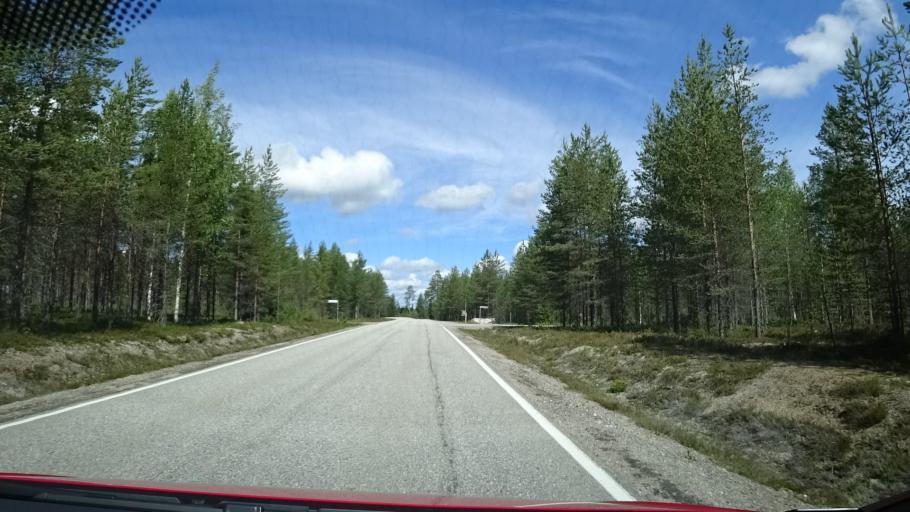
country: FI
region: Kainuu
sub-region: Kehys-Kainuu
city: Kuhmo
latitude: 64.6958
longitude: 29.6775
